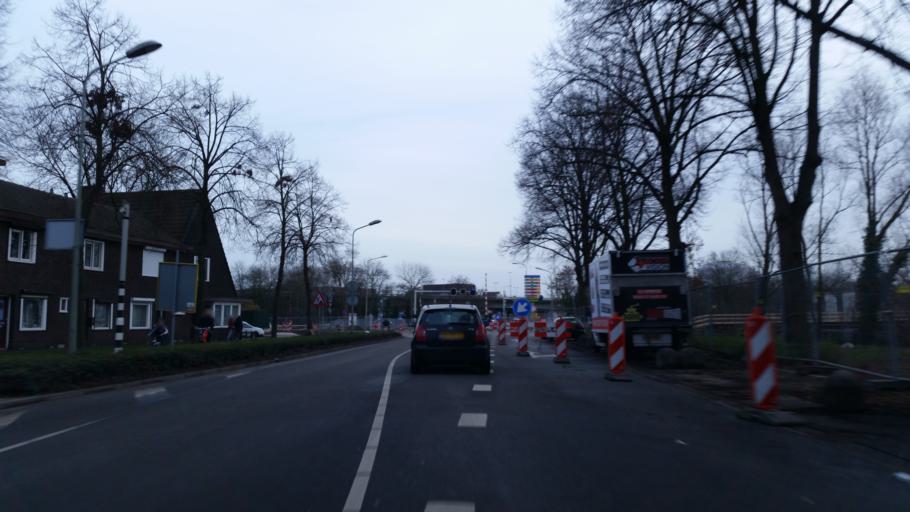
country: NL
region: Limburg
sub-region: Gemeente Maastricht
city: Maastricht
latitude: 50.8608
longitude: 5.6889
